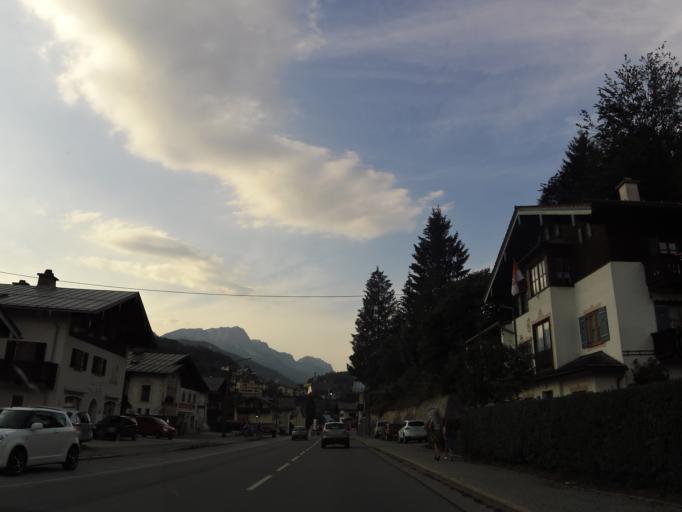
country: DE
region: Bavaria
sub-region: Upper Bavaria
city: Berchtesgaden
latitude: 47.6235
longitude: 13.0012
